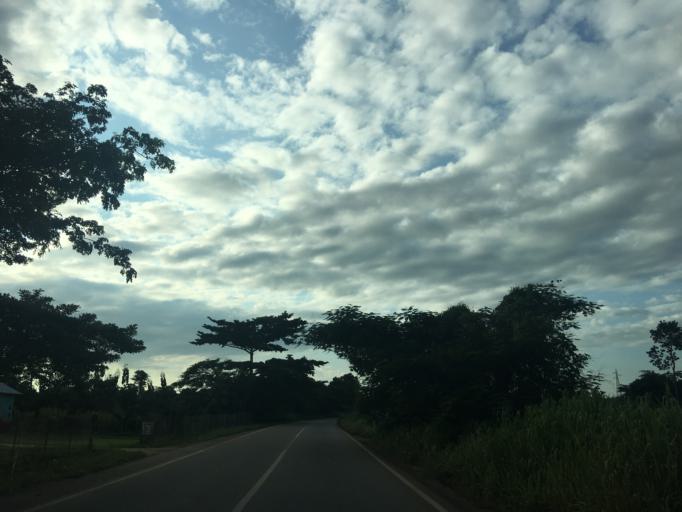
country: GH
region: Western
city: Bibiani
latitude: 6.3671
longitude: -2.2886
